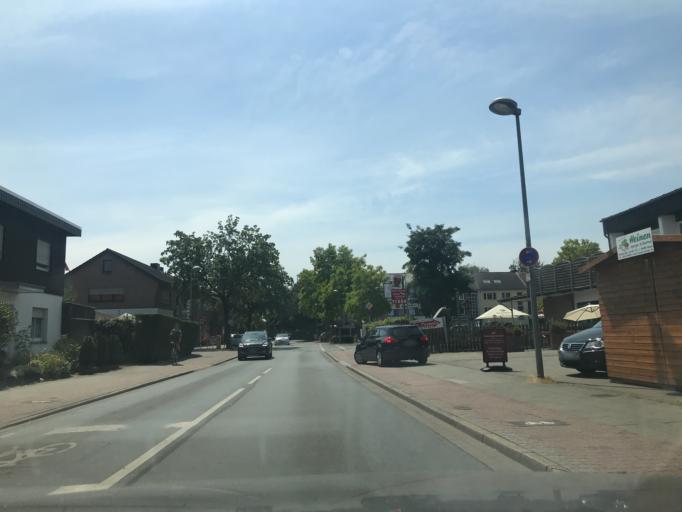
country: DE
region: North Rhine-Westphalia
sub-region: Regierungsbezirk Dusseldorf
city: Wesel
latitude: 51.6818
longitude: 6.5740
